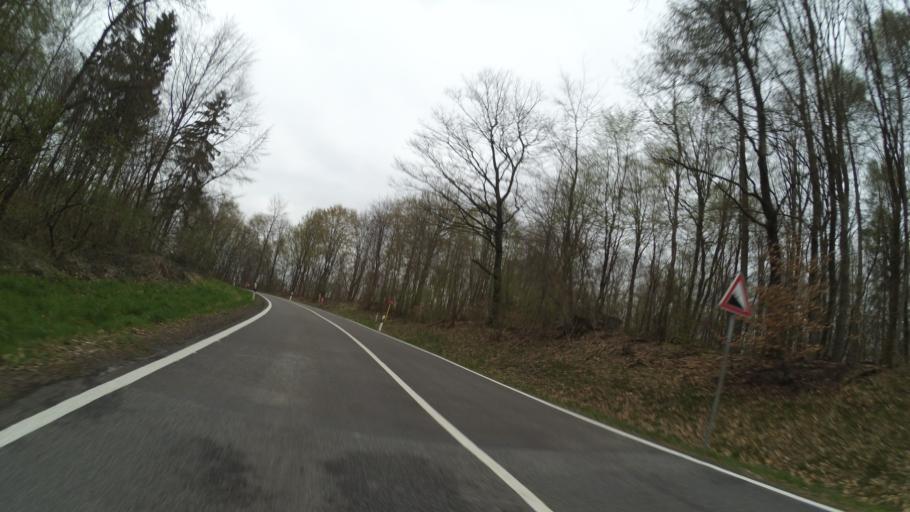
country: DE
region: Saarland
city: Friedrichsthal
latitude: 49.2977
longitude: 7.0926
